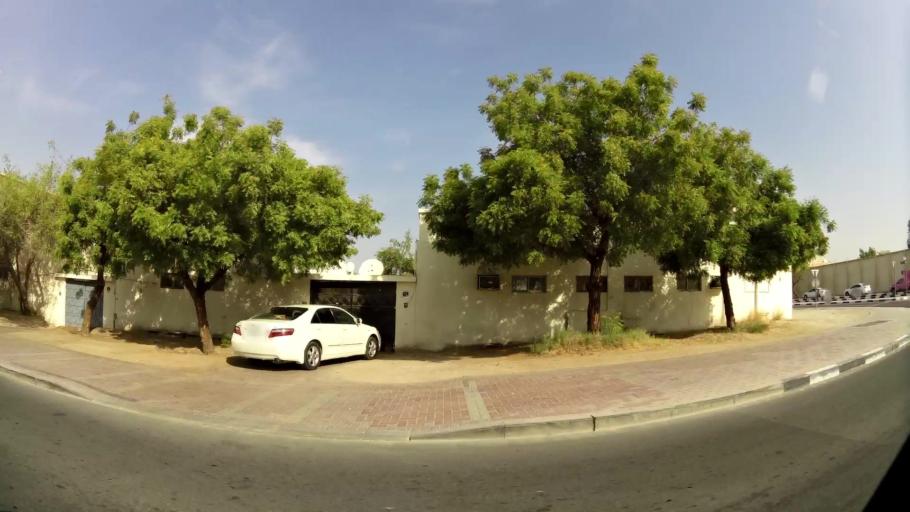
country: AE
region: Ash Shariqah
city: Sharjah
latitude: 25.2259
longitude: 55.3983
